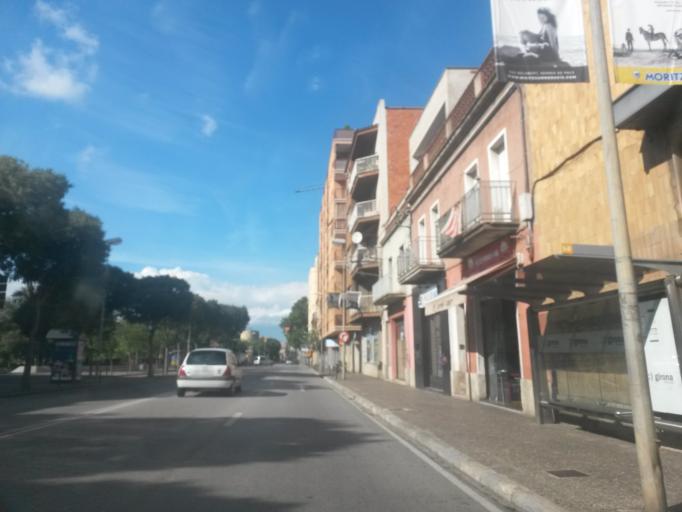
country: ES
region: Catalonia
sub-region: Provincia de Girona
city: Girona
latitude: 41.9710
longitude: 2.8148
